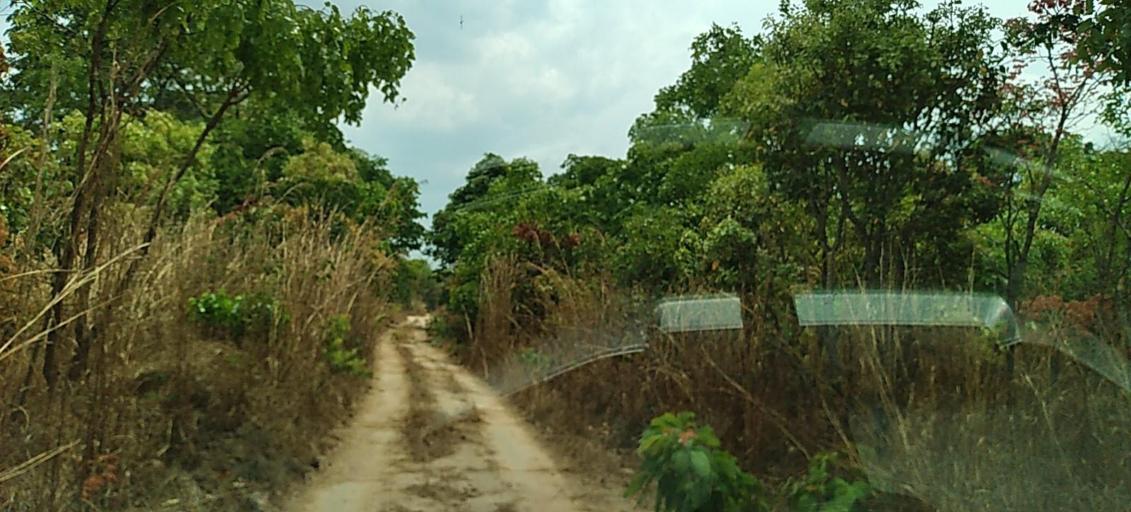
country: ZM
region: Copperbelt
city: Chililabombwe
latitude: -12.3297
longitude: 27.7690
